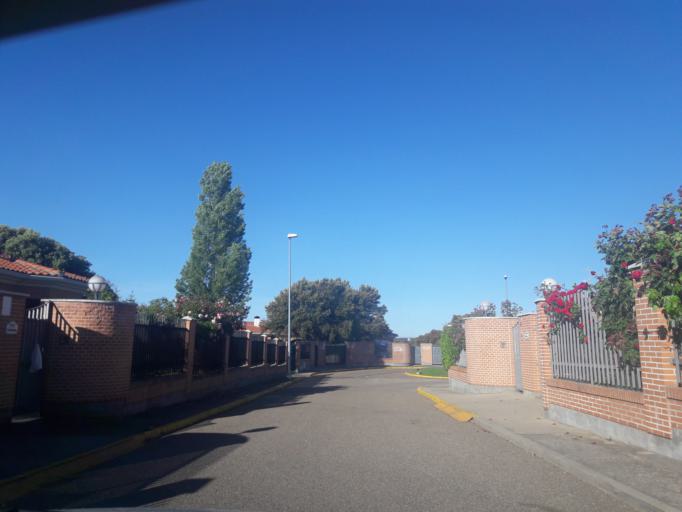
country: ES
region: Castille and Leon
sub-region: Provincia de Salamanca
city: Martinamor
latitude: 40.8041
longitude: -5.6348
